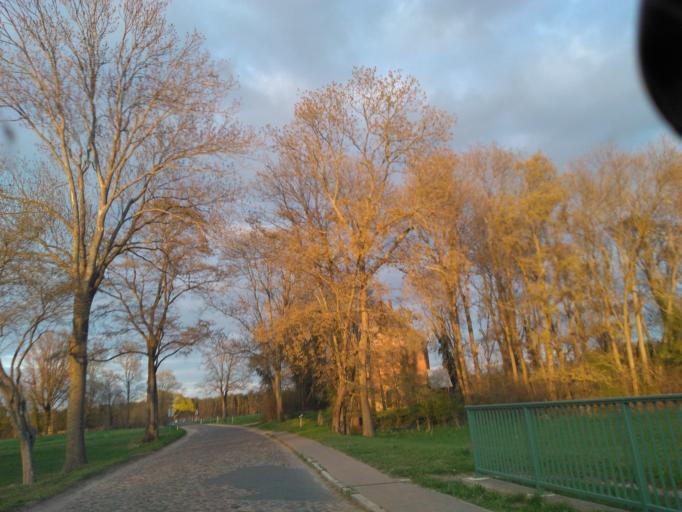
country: DE
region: Brandenburg
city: Buckow
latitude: 52.6069
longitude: 14.0360
